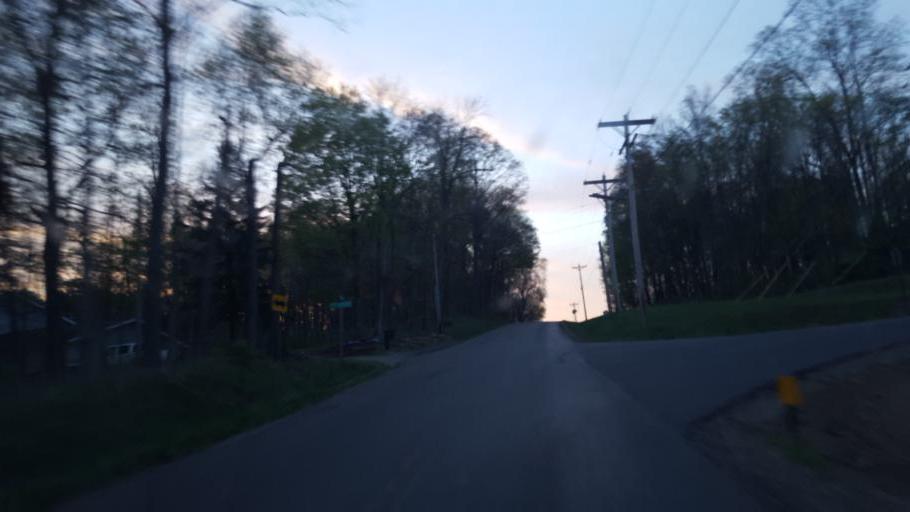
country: US
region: Ohio
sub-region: Knox County
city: Gambier
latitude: 40.4693
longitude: -82.3652
